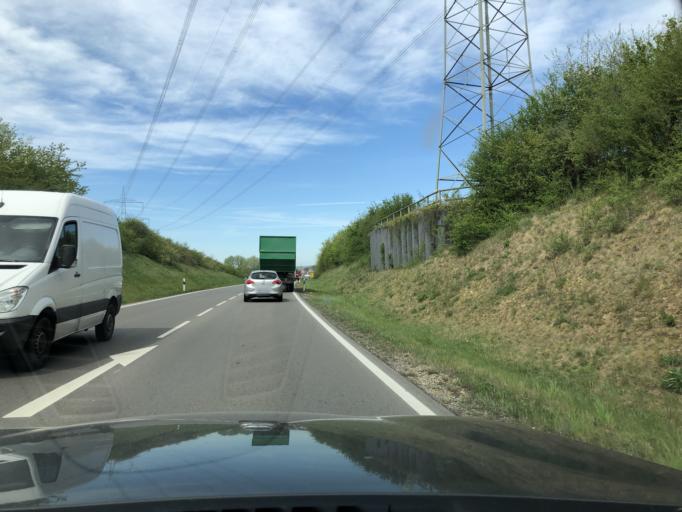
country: DE
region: Bavaria
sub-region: Swabia
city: Laugna
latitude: 48.5321
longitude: 10.7506
